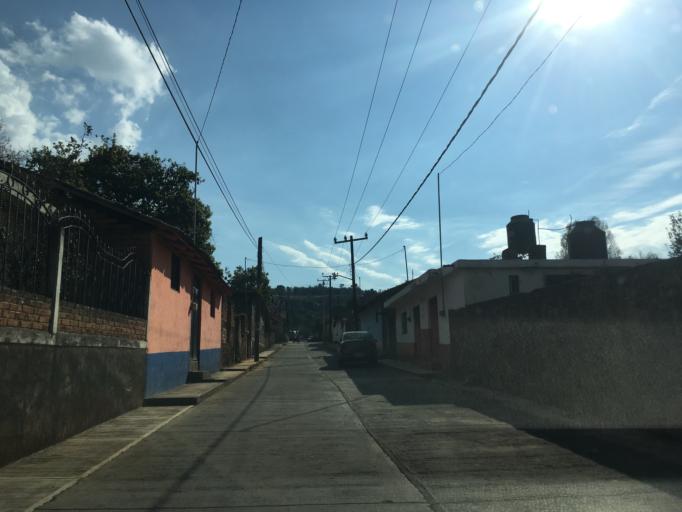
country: MX
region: Michoacan
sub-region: Patzcuaro
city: Santa Ana Chapitiro
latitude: 19.5271
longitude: -101.6538
